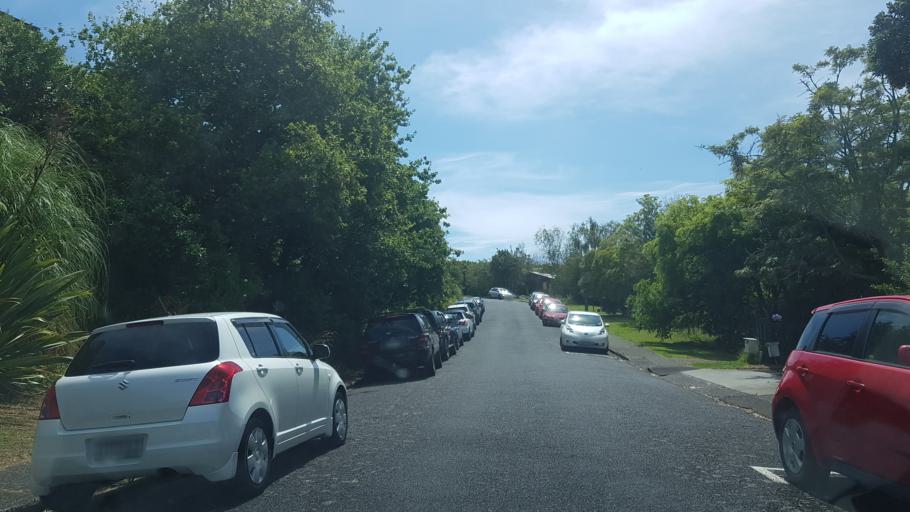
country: NZ
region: Auckland
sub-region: Auckland
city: North Shore
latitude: -36.7993
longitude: 174.7512
